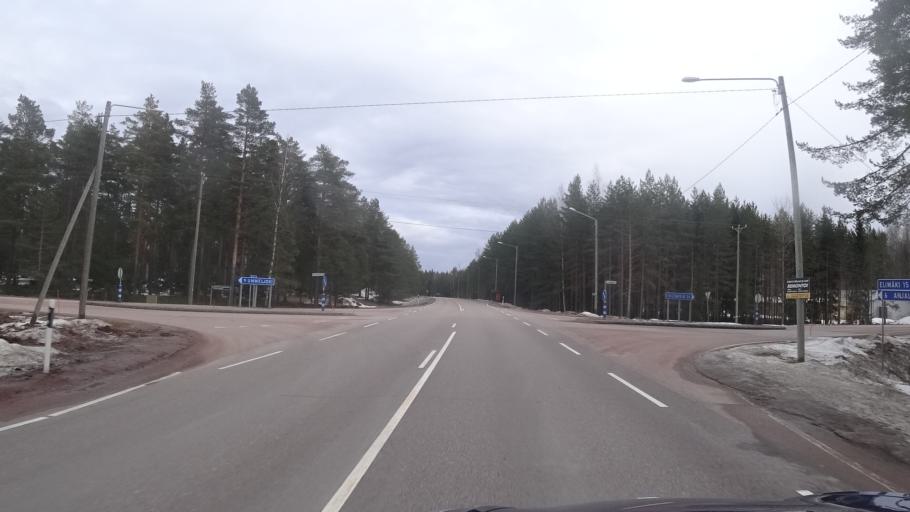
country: FI
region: Kymenlaakso
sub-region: Kouvola
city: Anjala
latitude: 60.6925
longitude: 26.6999
